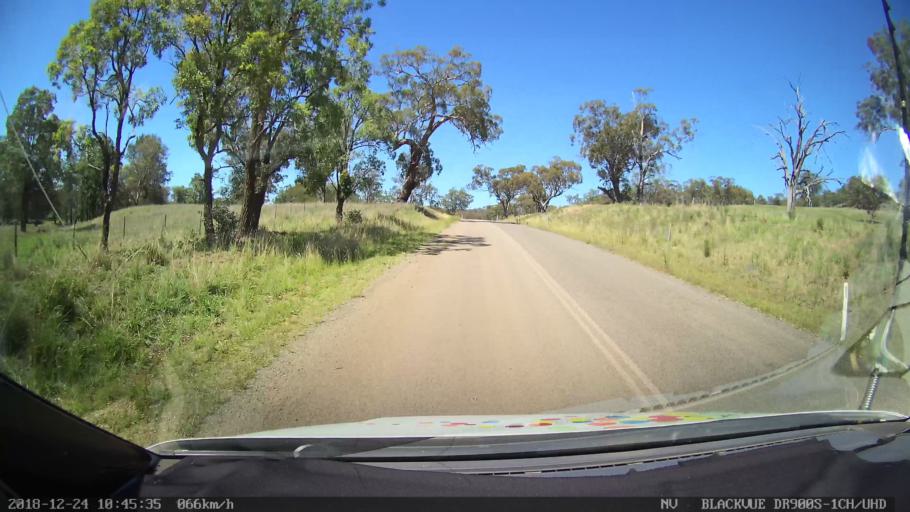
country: AU
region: New South Wales
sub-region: Upper Hunter Shire
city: Merriwa
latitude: -31.9042
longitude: 150.4348
